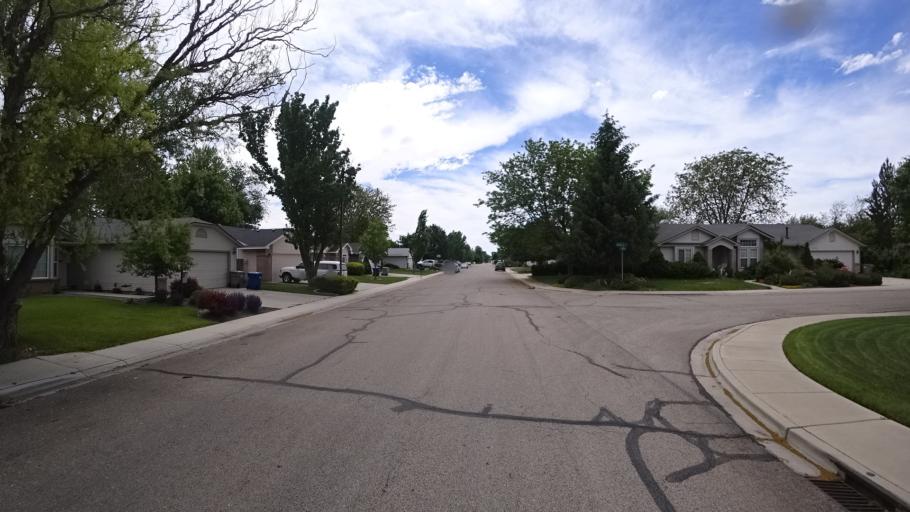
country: US
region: Idaho
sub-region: Ada County
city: Meridian
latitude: 43.6322
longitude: -116.3270
